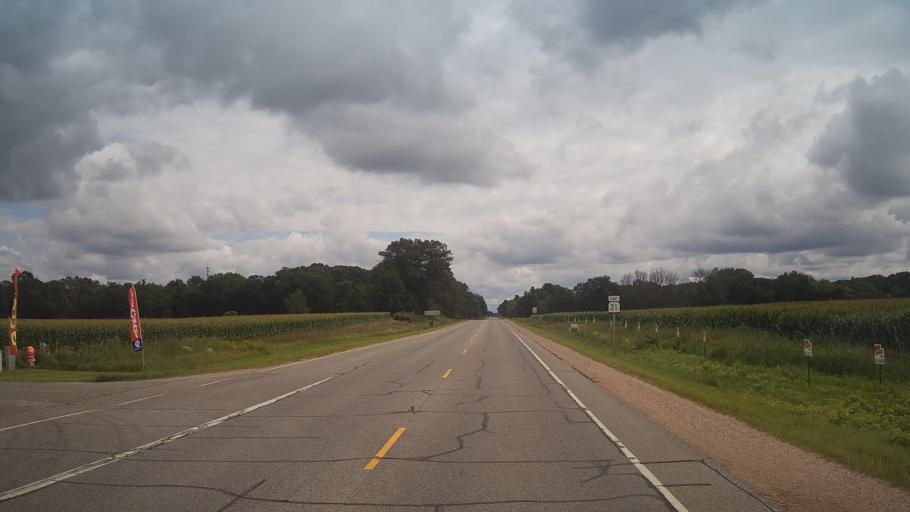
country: US
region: Wisconsin
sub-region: Adams County
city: Friendship
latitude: 44.0394
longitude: -89.9373
